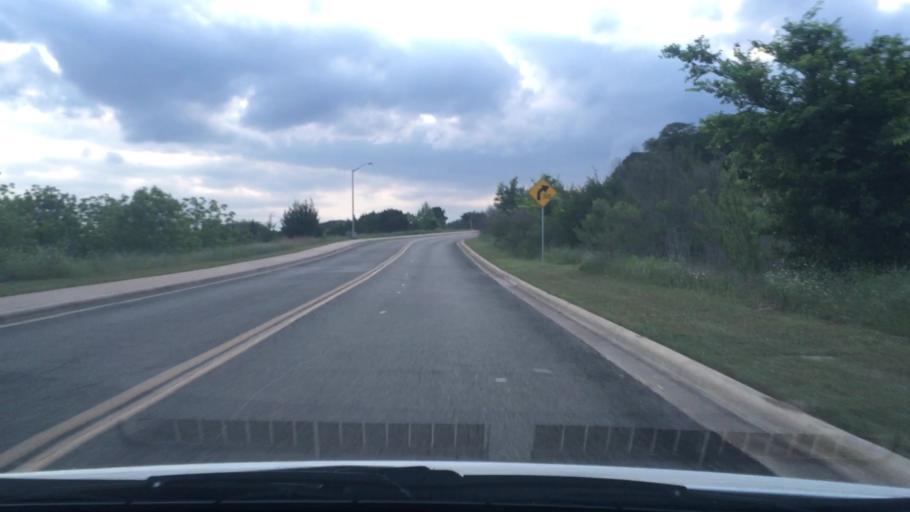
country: US
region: Texas
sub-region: Williamson County
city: Anderson Mill
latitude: 30.4512
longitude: -97.8552
